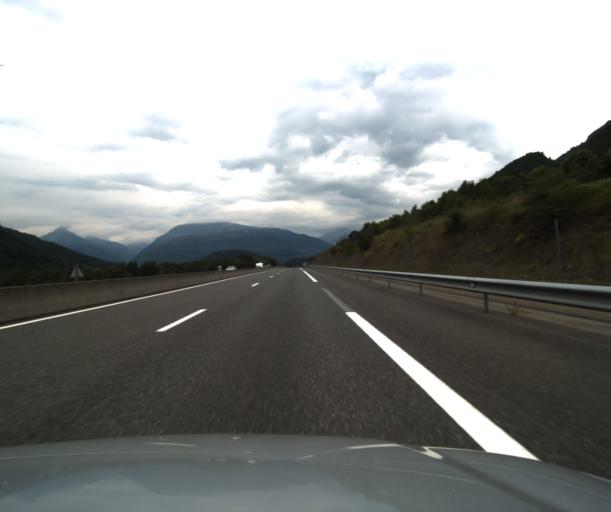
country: FR
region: Midi-Pyrenees
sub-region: Departement des Hautes-Pyrenees
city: Argeles-Gazost
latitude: 43.0457
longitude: -0.0601
